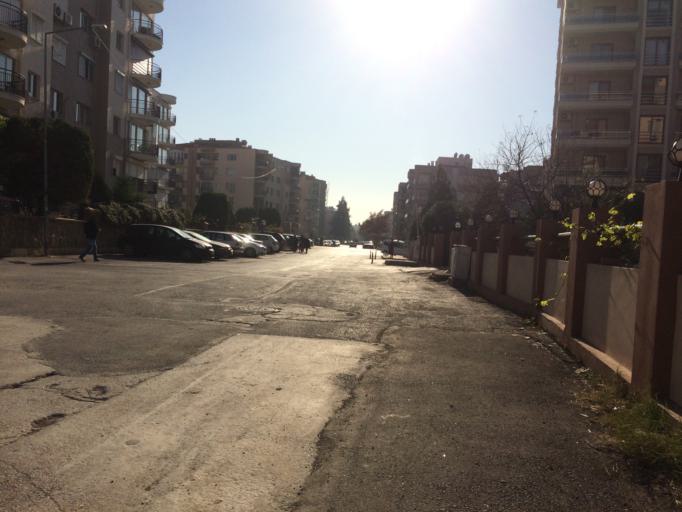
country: TR
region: Izmir
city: Karsiyaka
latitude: 38.4877
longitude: 27.0582
